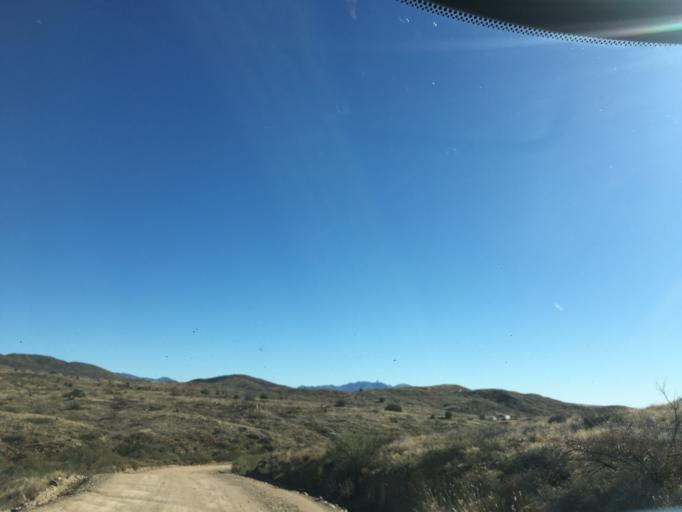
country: US
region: Arizona
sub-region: Yavapai County
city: Cordes Lakes
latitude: 34.2705
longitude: -112.1085
